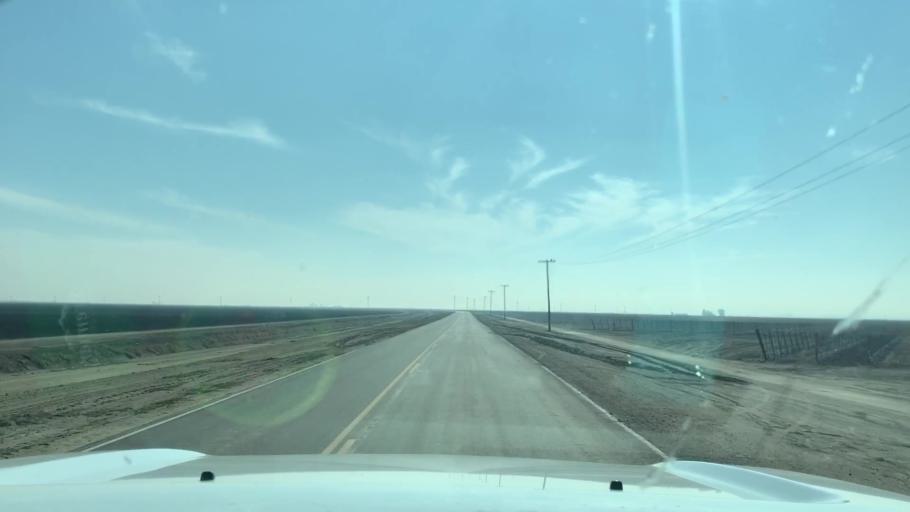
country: US
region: California
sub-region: Kern County
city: Buttonwillow
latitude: 35.4827
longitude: -119.5920
